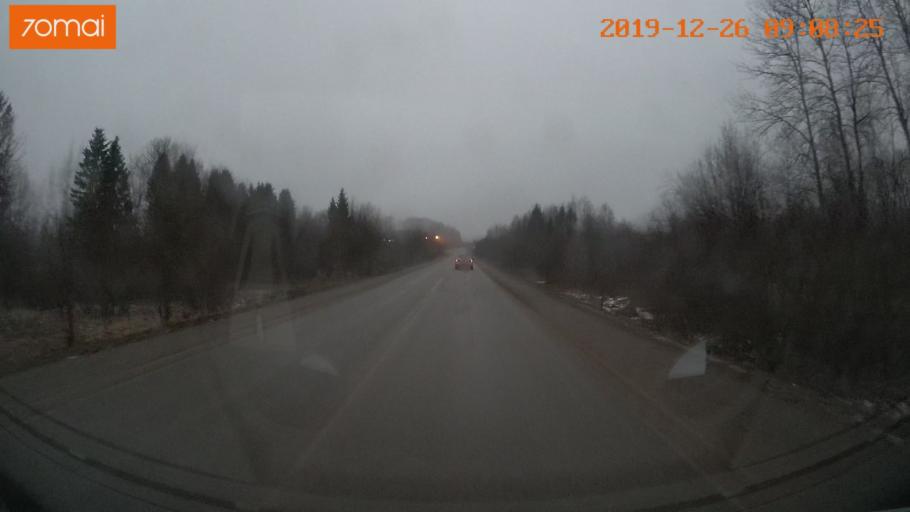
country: RU
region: Vologda
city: Gryazovets
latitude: 58.8564
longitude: 40.2483
